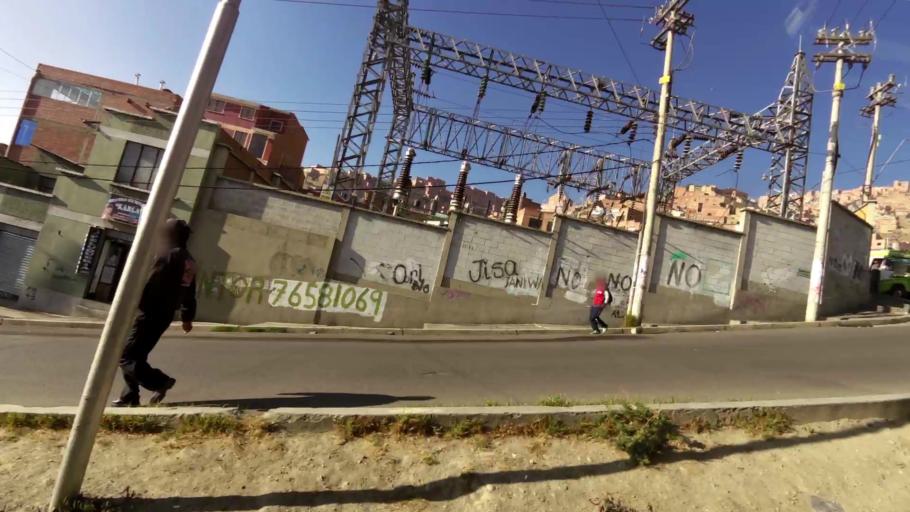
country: BO
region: La Paz
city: La Paz
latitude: -16.5006
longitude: -68.1538
